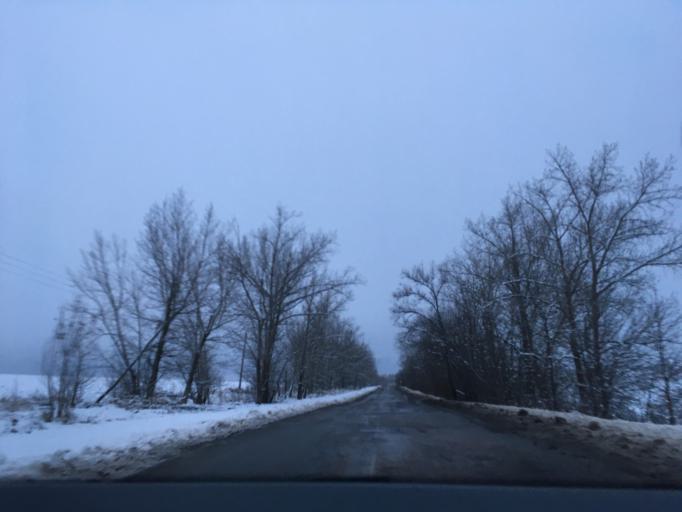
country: RU
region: Voronezj
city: Verkhniy Mamon
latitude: 50.0542
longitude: 40.2511
